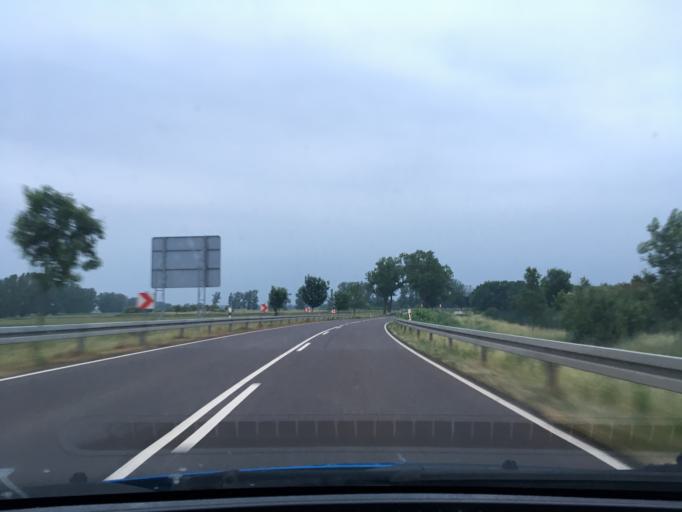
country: DE
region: Saxony-Anhalt
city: Salzwedel
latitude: 52.8730
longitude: 11.1639
